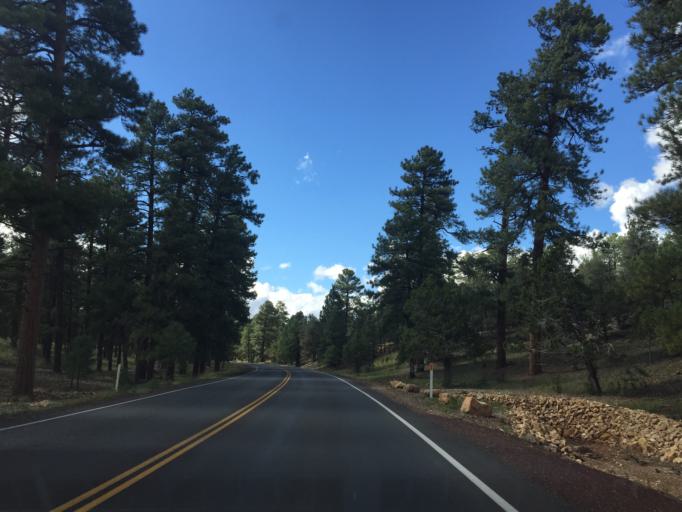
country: US
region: Arizona
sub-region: Coconino County
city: Grand Canyon
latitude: 36.0549
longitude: -112.1278
